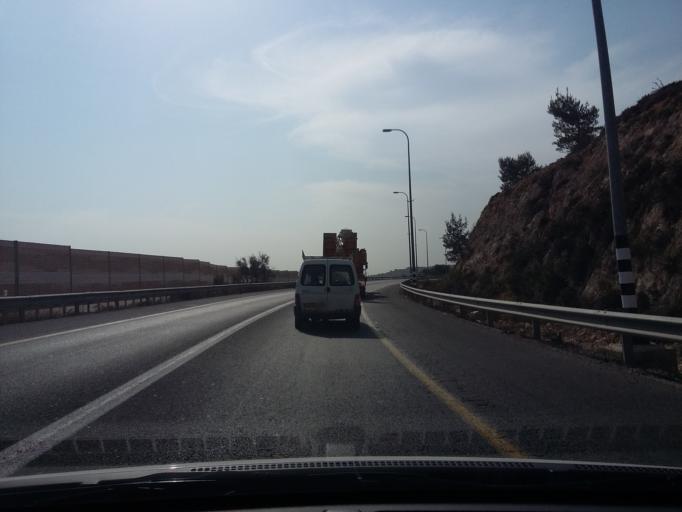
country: PS
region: West Bank
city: Al Khadir
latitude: 31.6927
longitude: 35.1610
